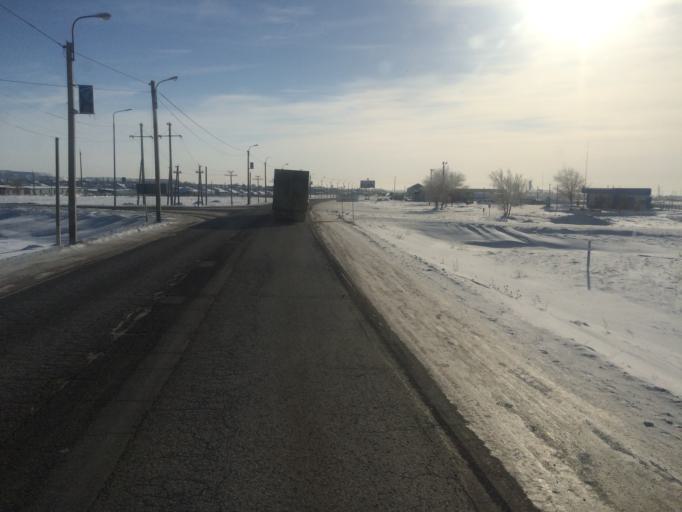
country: KZ
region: Aqtoebe
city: Khromtau
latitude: 50.2578
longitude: 58.4114
